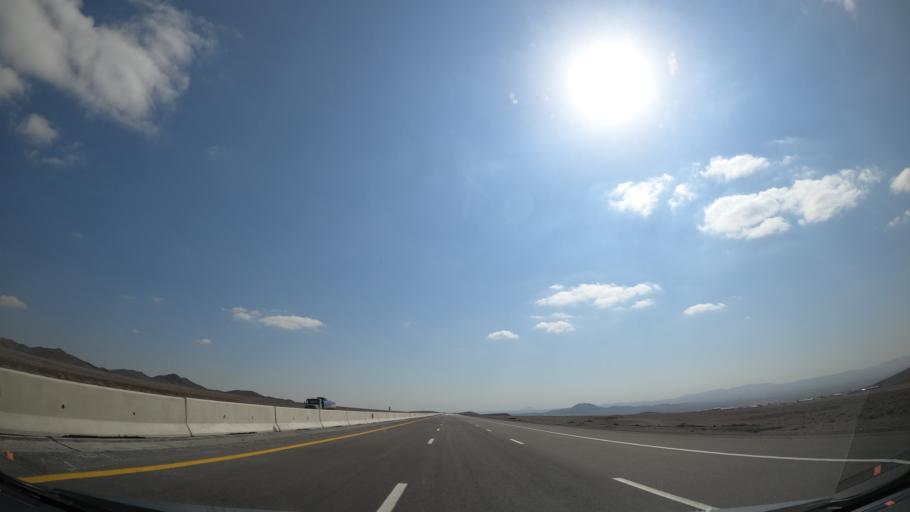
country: IR
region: Alborz
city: Nazarabad
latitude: 35.6755
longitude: 50.6443
